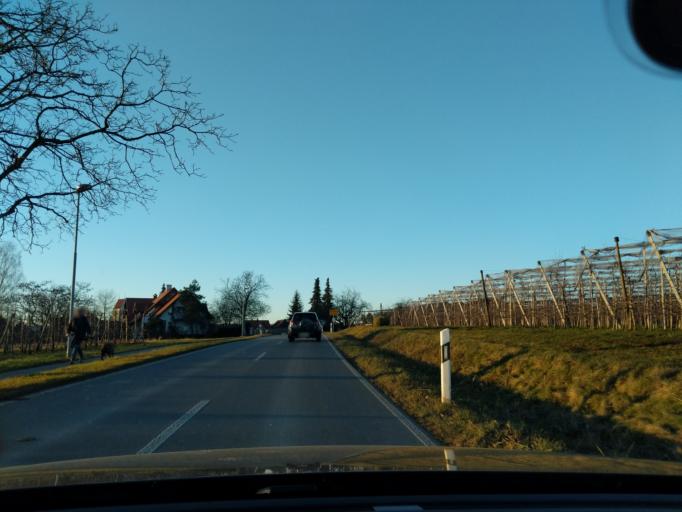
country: DE
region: Baden-Wuerttemberg
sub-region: Tuebingen Region
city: Immenstaad am Bodensee
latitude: 47.6713
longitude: 9.3557
